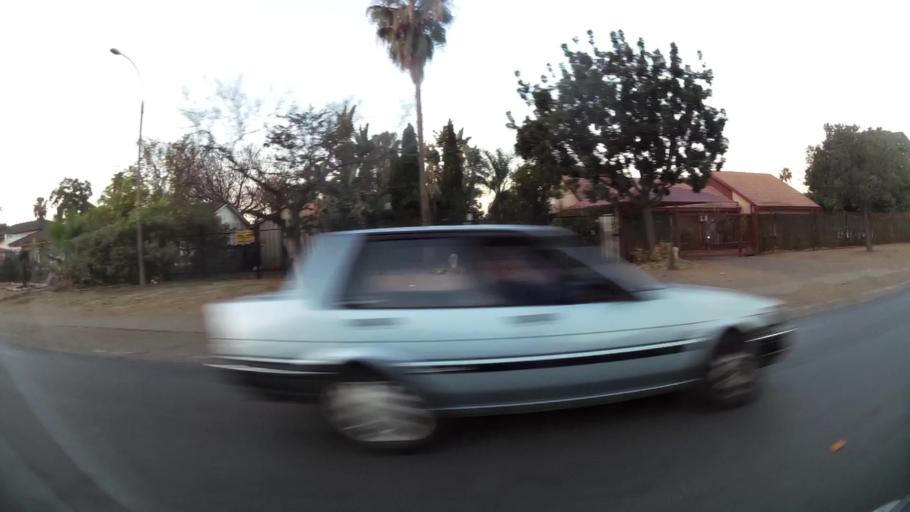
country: ZA
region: North-West
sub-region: Bojanala Platinum District Municipality
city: Rustenburg
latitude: -25.6591
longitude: 27.2468
